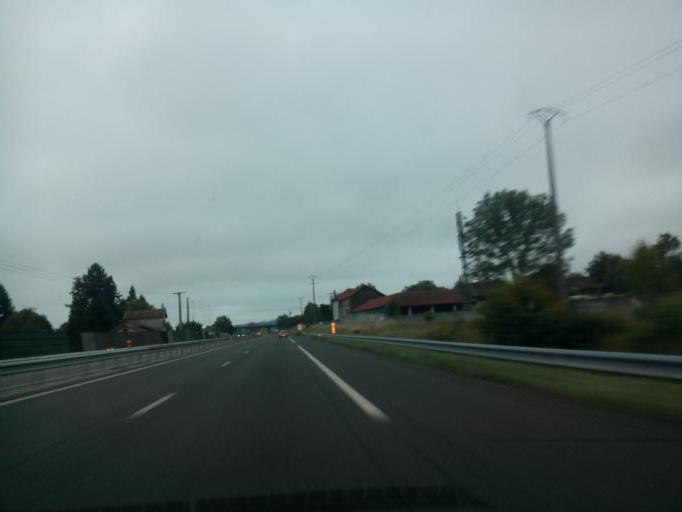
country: FR
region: Rhone-Alpes
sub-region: Departement de l'Isere
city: Cessieu
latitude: 45.5624
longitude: 5.3726
